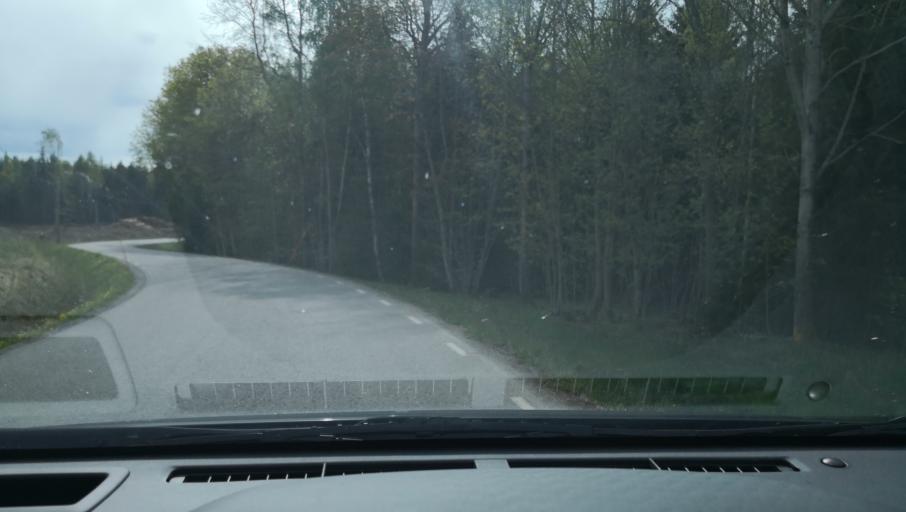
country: SE
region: OErebro
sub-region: Kumla Kommun
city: Hallabrottet
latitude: 59.1647
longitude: 15.2505
